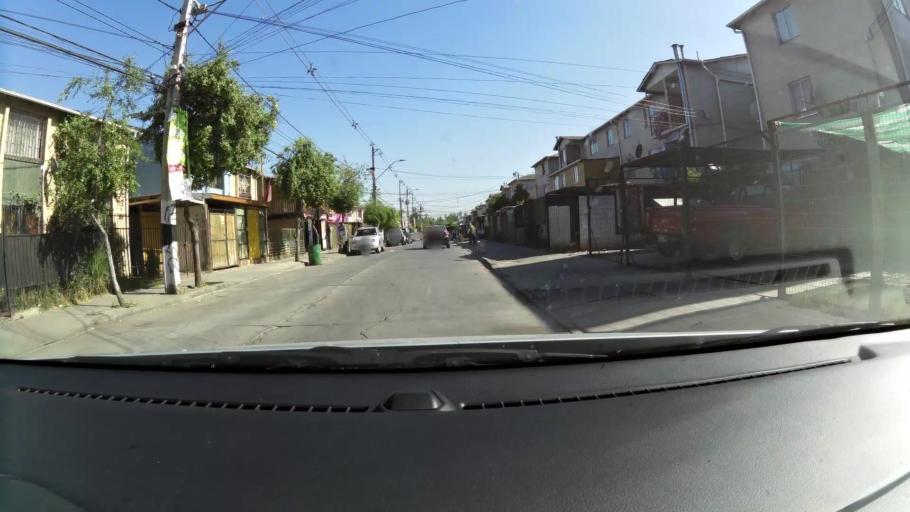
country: CL
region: Santiago Metropolitan
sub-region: Provincia de Maipo
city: San Bernardo
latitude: -33.5661
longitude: -70.7050
